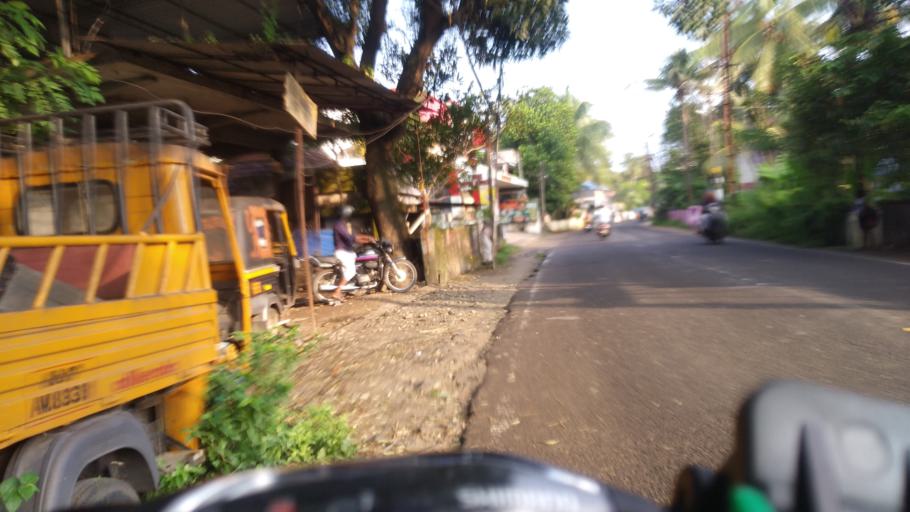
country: IN
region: Kerala
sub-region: Ernakulam
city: Elur
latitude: 10.0620
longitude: 76.2135
